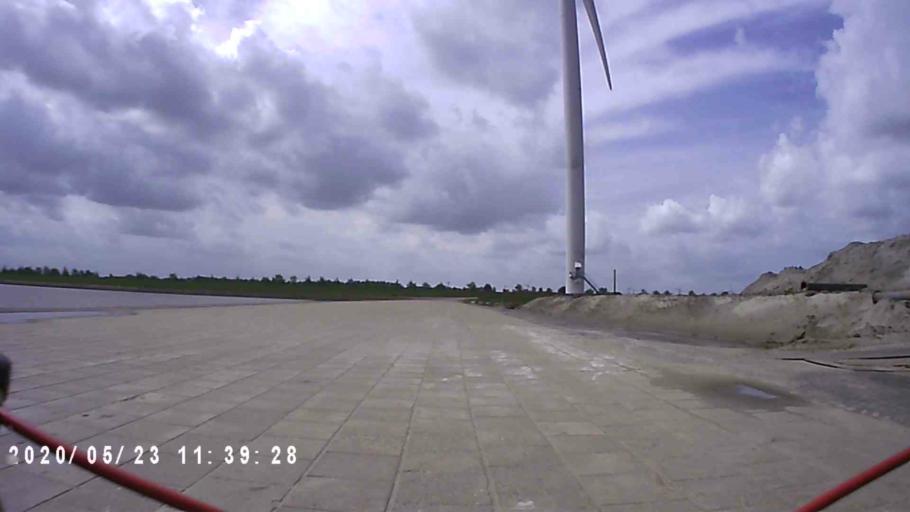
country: NL
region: Groningen
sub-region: Gemeente Delfzijl
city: Delfzijl
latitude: 53.3087
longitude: 7.0111
